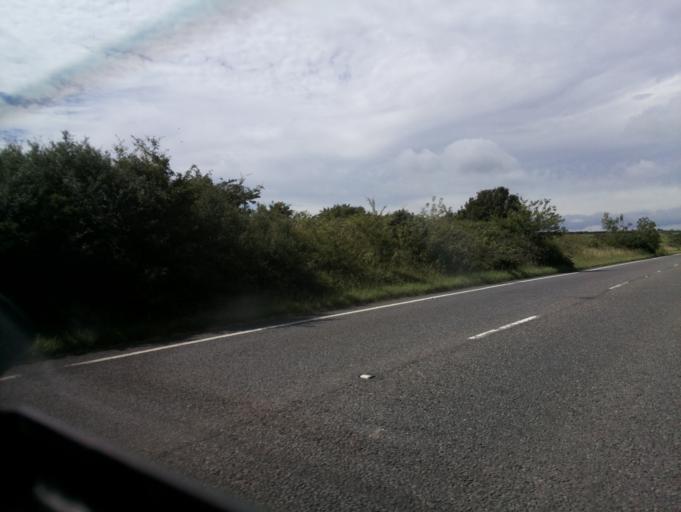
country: GB
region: England
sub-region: Dorset
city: Dorchester
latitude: 50.7847
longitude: -2.5424
